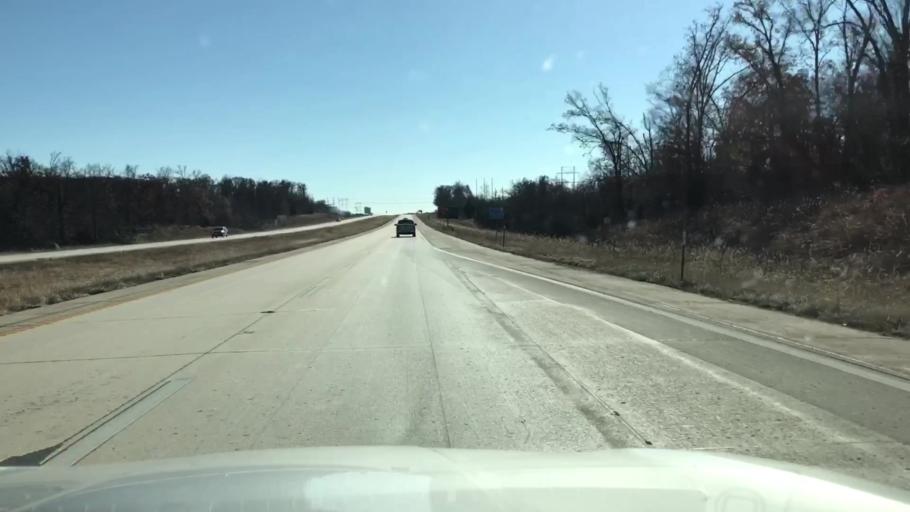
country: US
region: Missouri
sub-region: Jasper County
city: Duenweg
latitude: 37.0486
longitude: -94.4274
